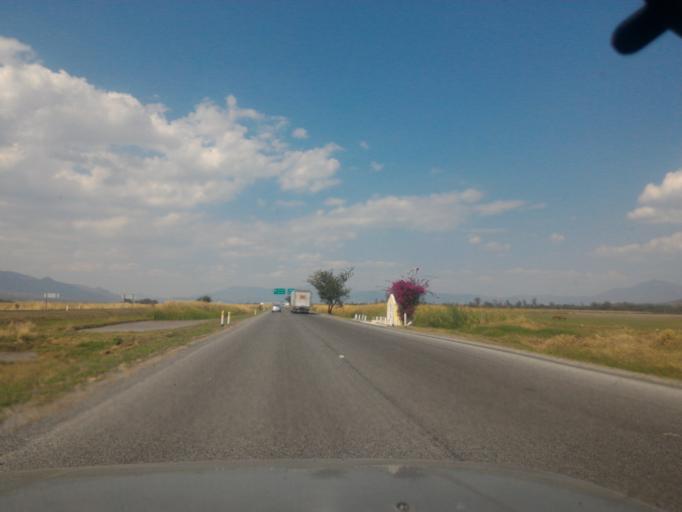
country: MX
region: Jalisco
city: Atoyac
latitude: 19.9989
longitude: -103.5357
